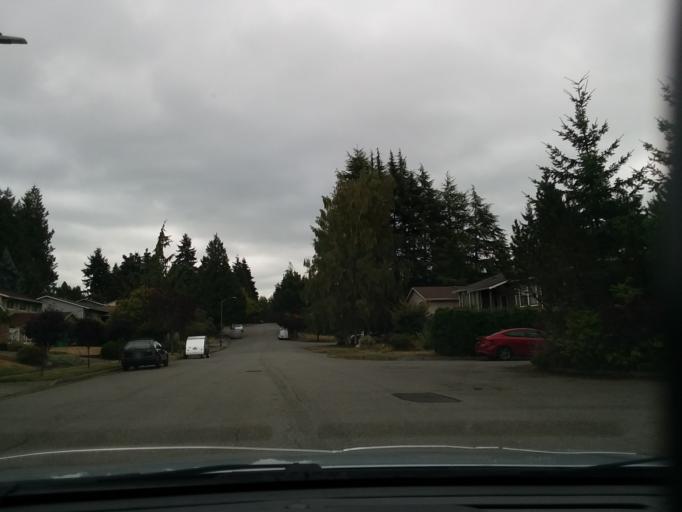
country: US
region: Washington
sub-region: Snohomish County
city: Alderwood Manor
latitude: 47.8249
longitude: -122.2904
